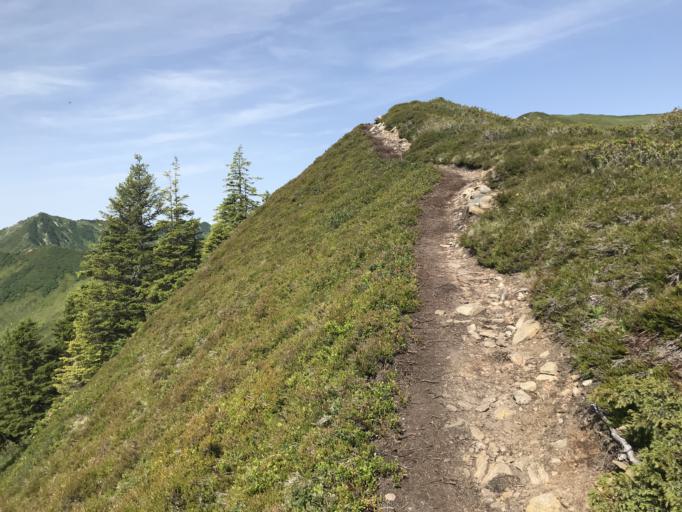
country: AT
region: Vorarlberg
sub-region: Politischer Bezirk Bregenz
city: Damuels
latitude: 47.2862
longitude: 9.8553
